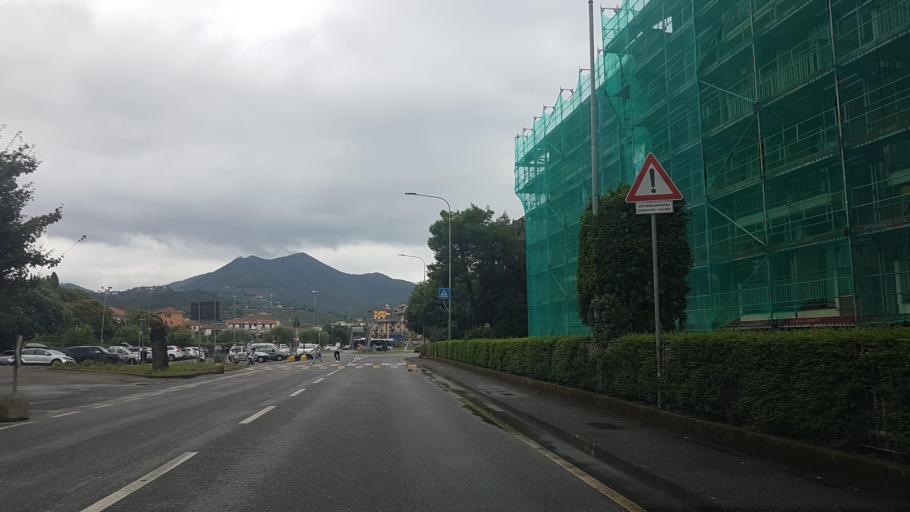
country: IT
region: Liguria
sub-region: Provincia di Genova
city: Sestri Levante
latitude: 44.2728
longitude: 9.4181
